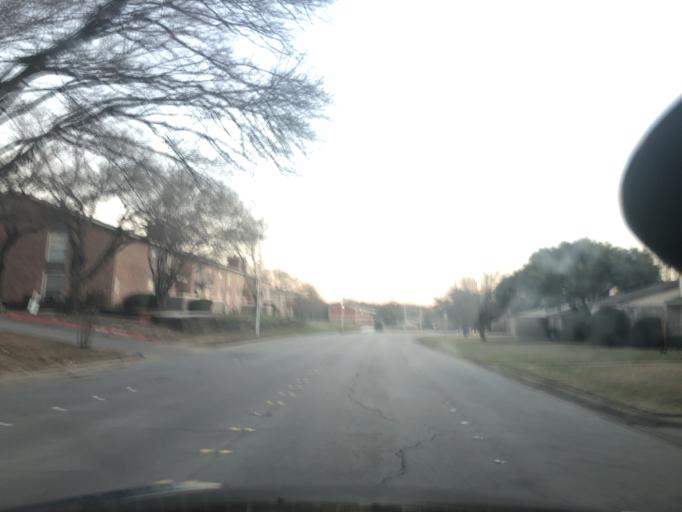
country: US
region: Texas
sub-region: Tarrant County
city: White Settlement
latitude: 32.7310
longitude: -97.4689
